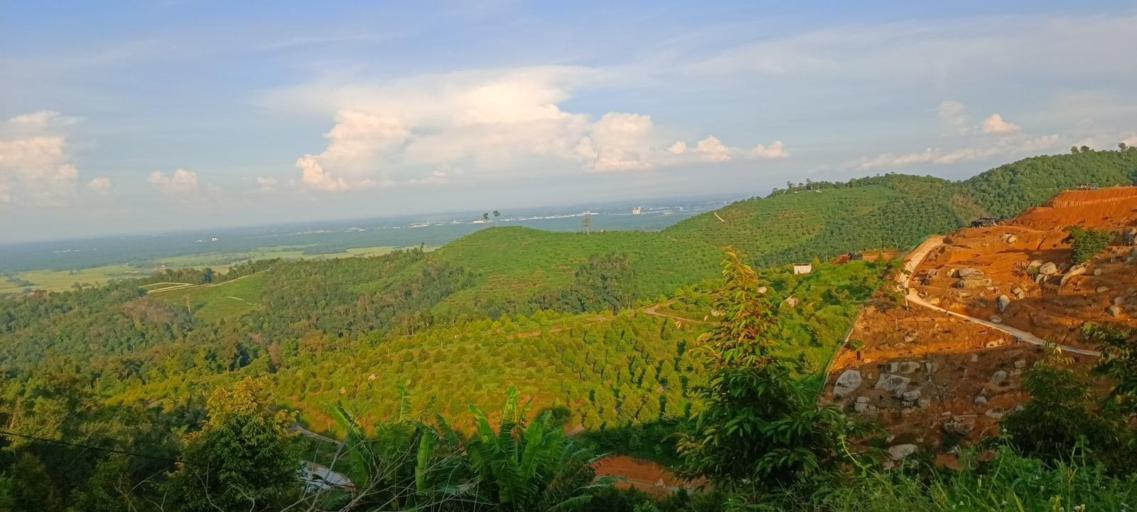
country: MY
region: Perak
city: Parit Buntar
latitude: 5.1258
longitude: 100.5519
